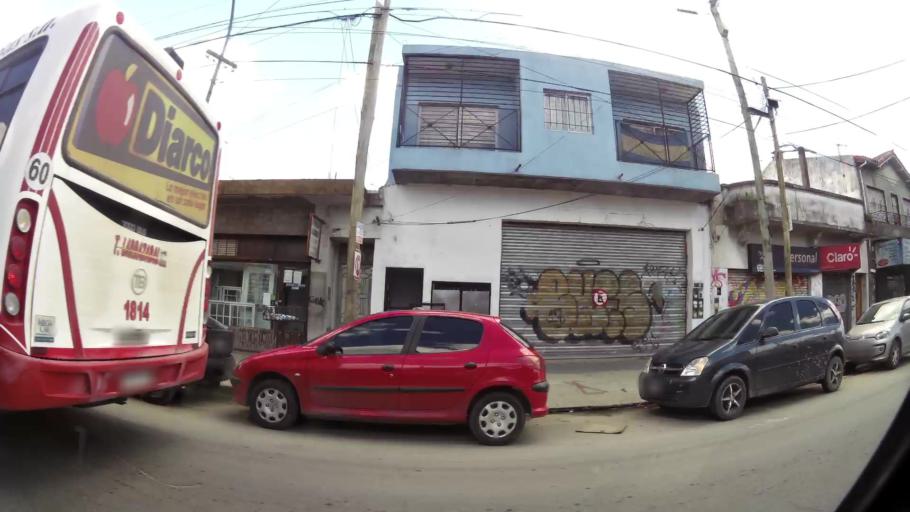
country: AR
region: Buenos Aires
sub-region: Partido de Lanus
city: Lanus
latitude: -34.7105
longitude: -58.4227
